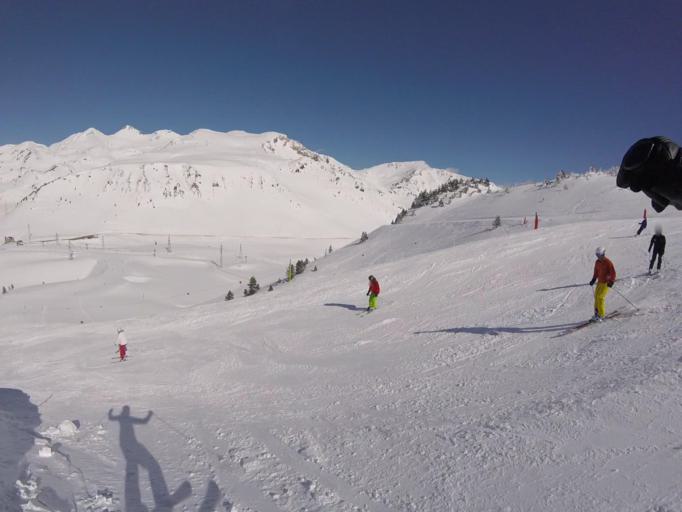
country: ES
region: Catalonia
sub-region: Provincia de Lleida
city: Espot
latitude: 42.6571
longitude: 0.9815
